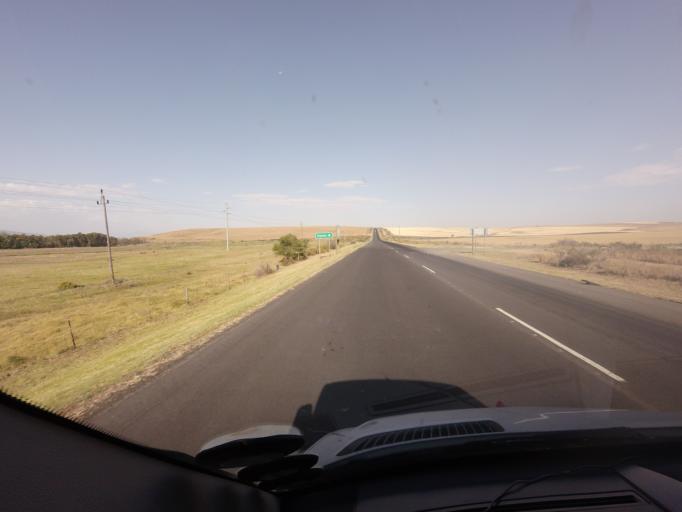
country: ZA
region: Western Cape
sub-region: Cape Winelands District Municipality
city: Ashton
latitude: -34.1559
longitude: 19.9409
